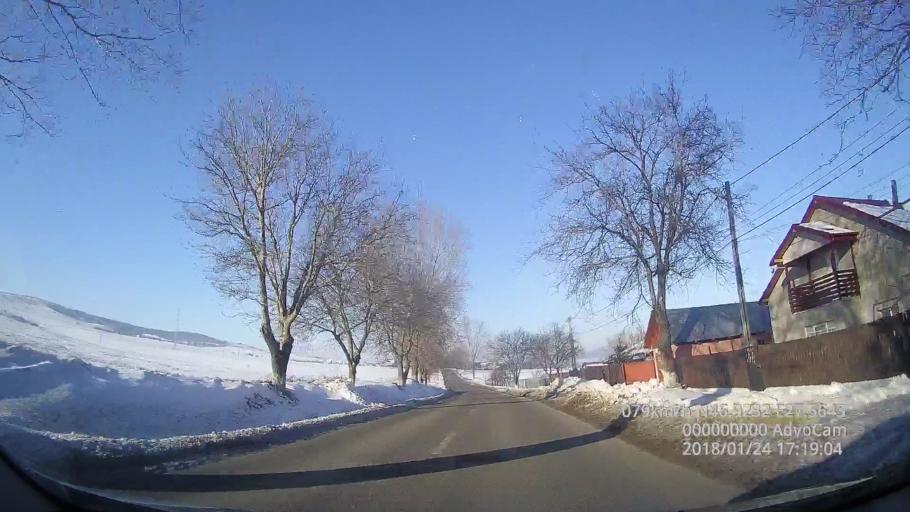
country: RO
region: Iasi
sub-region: Comuna Scanteia
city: Scanteia
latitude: 46.9237
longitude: 27.5643
